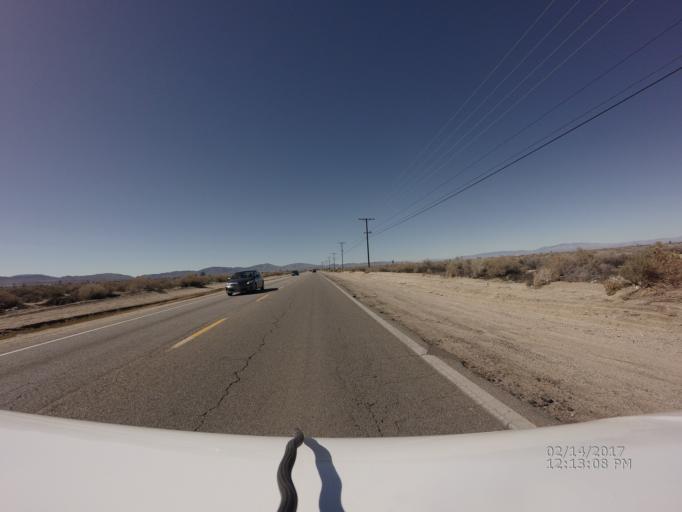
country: US
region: California
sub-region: Los Angeles County
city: Littlerock
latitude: 34.5797
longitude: -117.9815
